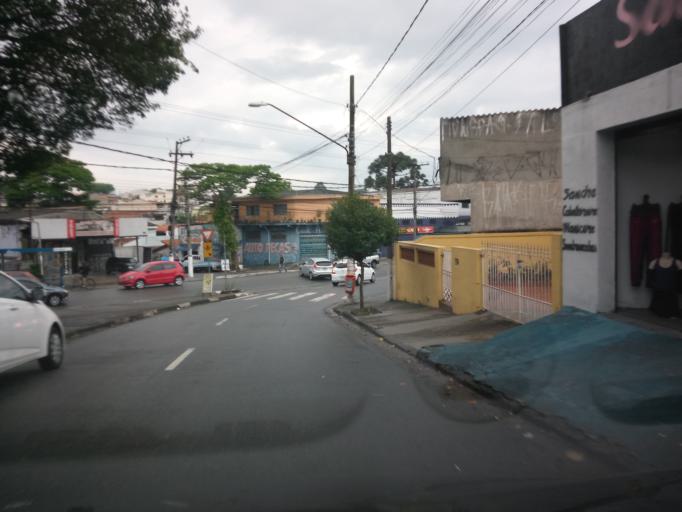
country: BR
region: Sao Paulo
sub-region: Sao Bernardo Do Campo
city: Sao Bernardo do Campo
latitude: -23.7191
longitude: -46.5826
